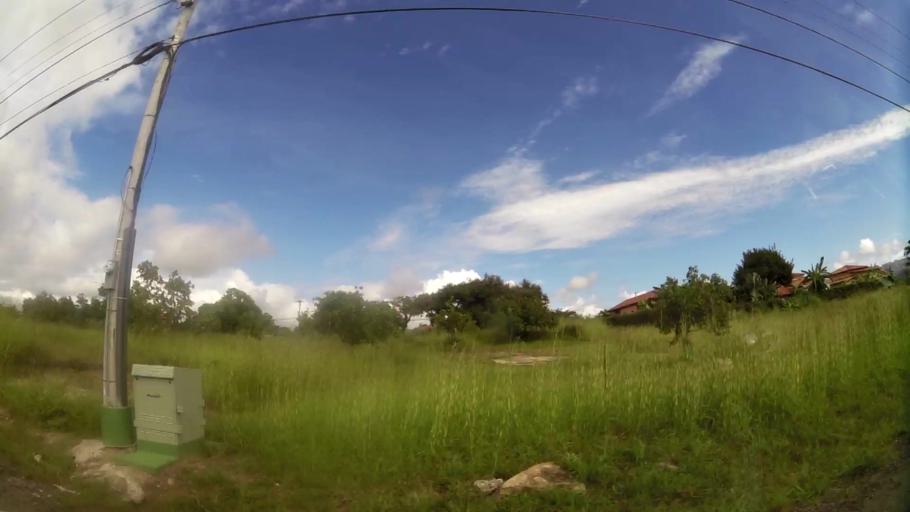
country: PA
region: Panama
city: Nueva Gorgona
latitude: 8.5451
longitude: -79.8939
